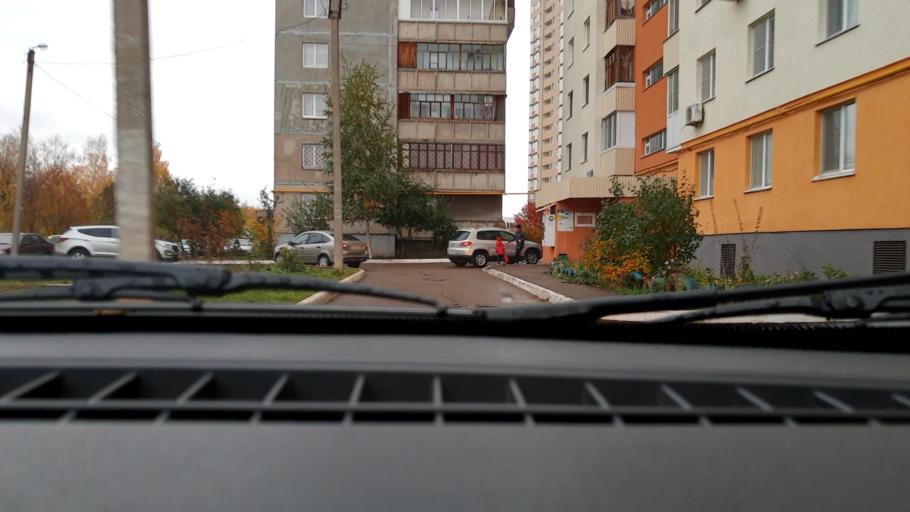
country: RU
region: Bashkortostan
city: Mikhaylovka
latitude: 54.7902
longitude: 55.8677
